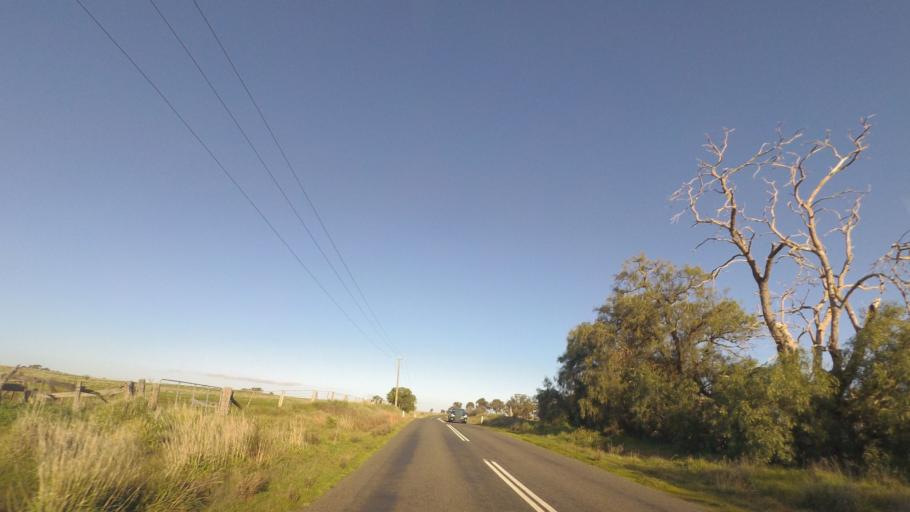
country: AU
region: Victoria
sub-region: Greater Bendigo
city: Kennington
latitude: -36.8176
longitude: 144.5142
